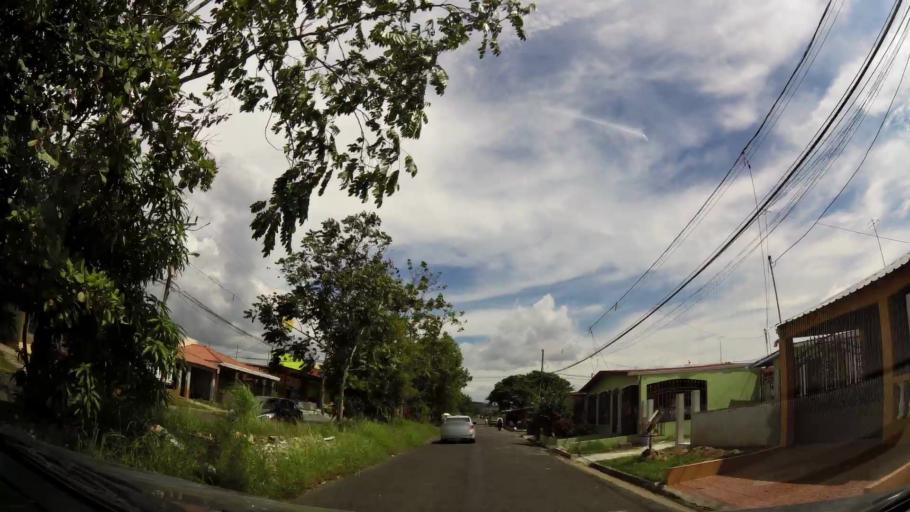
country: PA
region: Panama
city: Nuevo Arraijan
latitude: 8.9085
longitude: -79.7126
